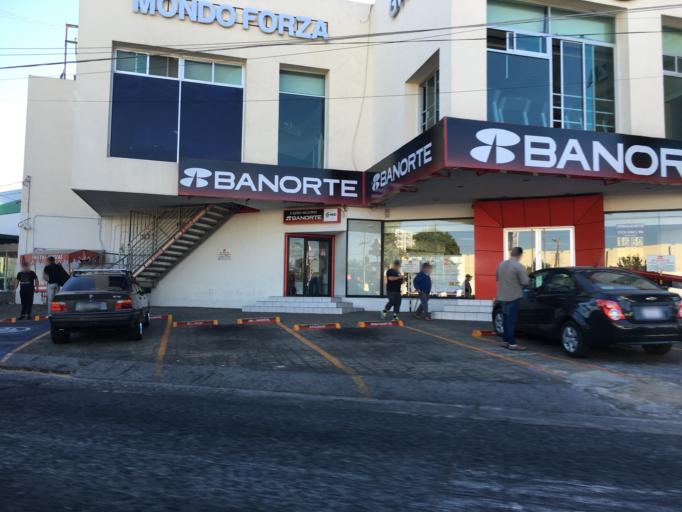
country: MX
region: Jalisco
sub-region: Zapopan
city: Zapopan
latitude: 20.7055
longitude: -103.3482
